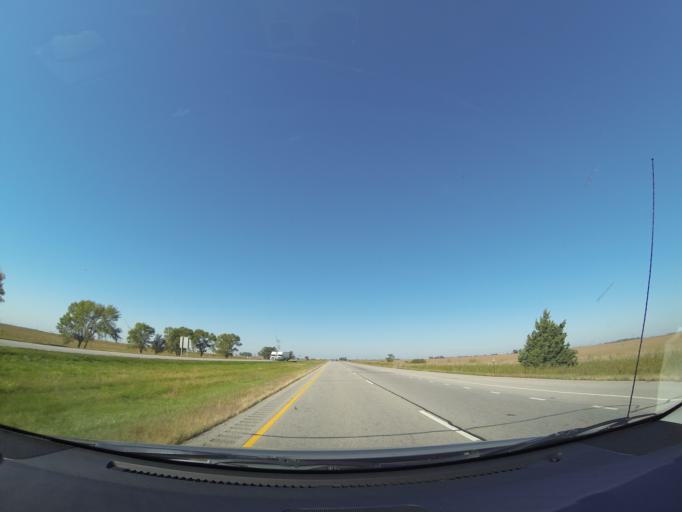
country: US
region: Nebraska
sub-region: Seward County
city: Seward
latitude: 40.8226
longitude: -97.2222
